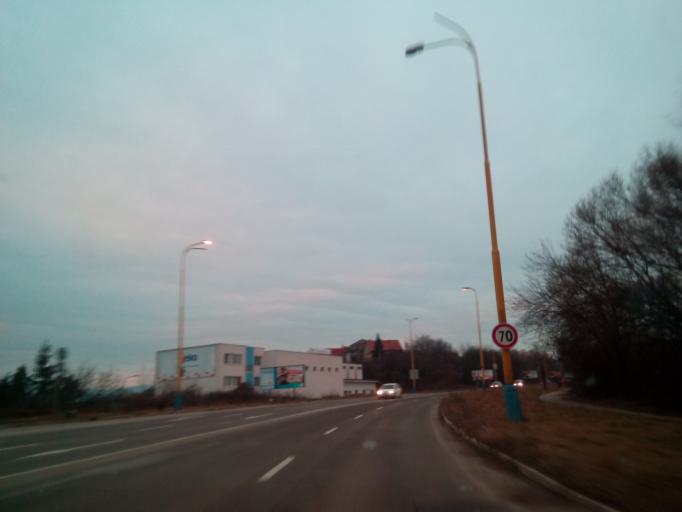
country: SK
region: Kosicky
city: Kosice
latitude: 48.7019
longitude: 21.2200
